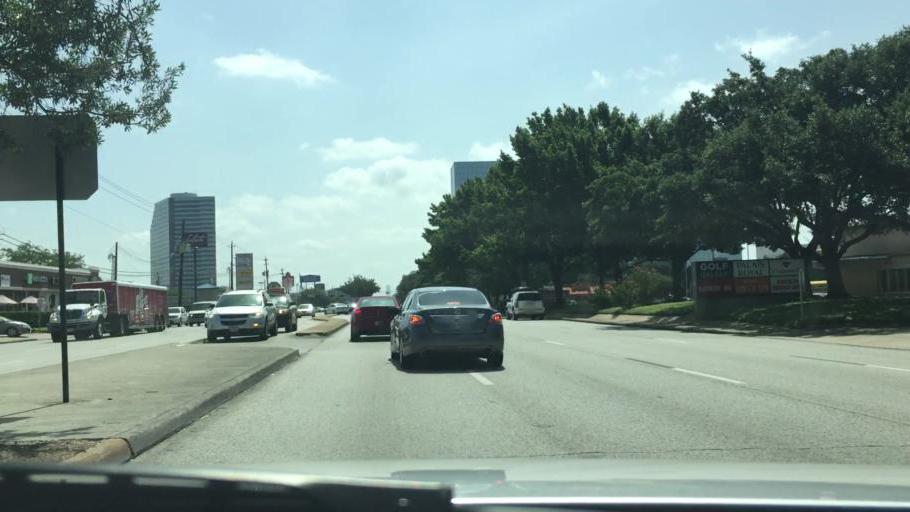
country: US
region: Texas
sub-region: Harris County
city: Bunker Hill Village
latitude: 29.7367
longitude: -95.5698
